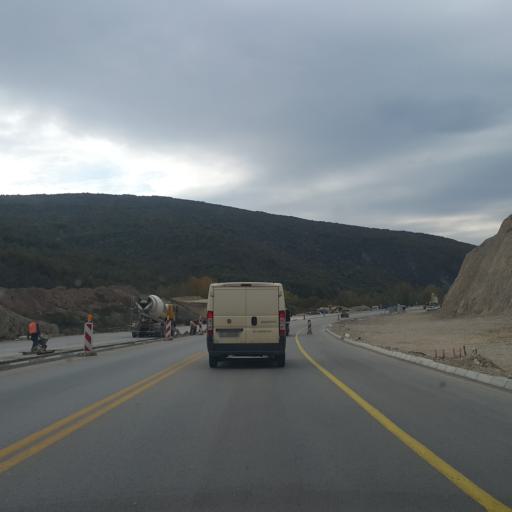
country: RS
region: Central Serbia
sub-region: Pirotski Okrug
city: Bela Palanka
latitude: 43.2246
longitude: 22.4291
